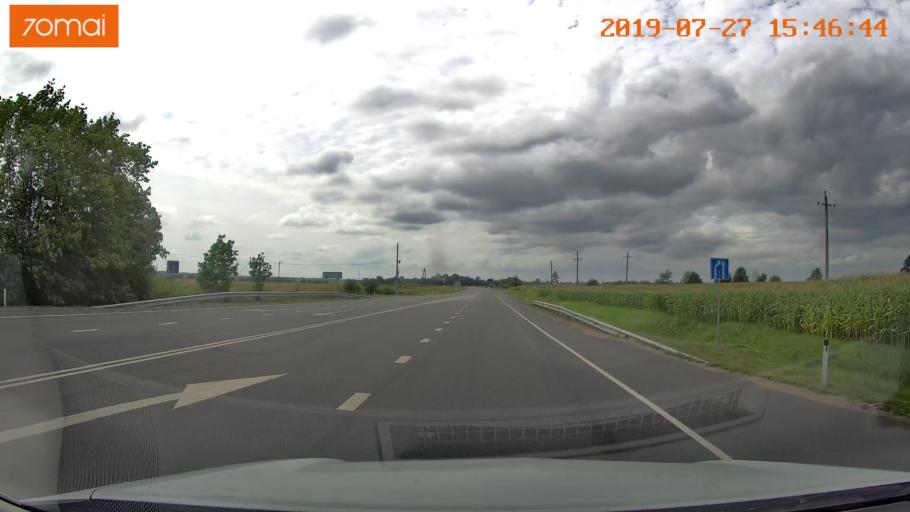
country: RU
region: Kaliningrad
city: Gusev
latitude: 54.6034
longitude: 22.1059
